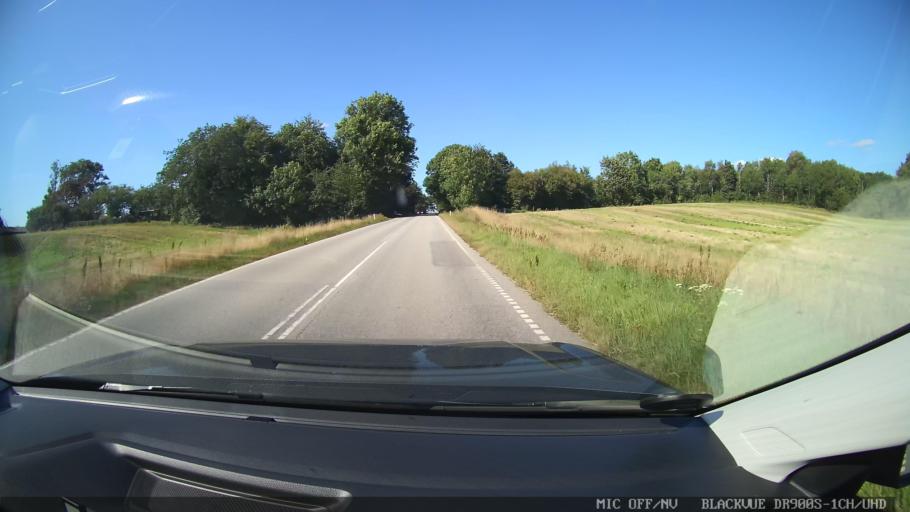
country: DK
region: North Denmark
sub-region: Mariagerfjord Kommune
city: Mariager
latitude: 56.6232
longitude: 9.9802
